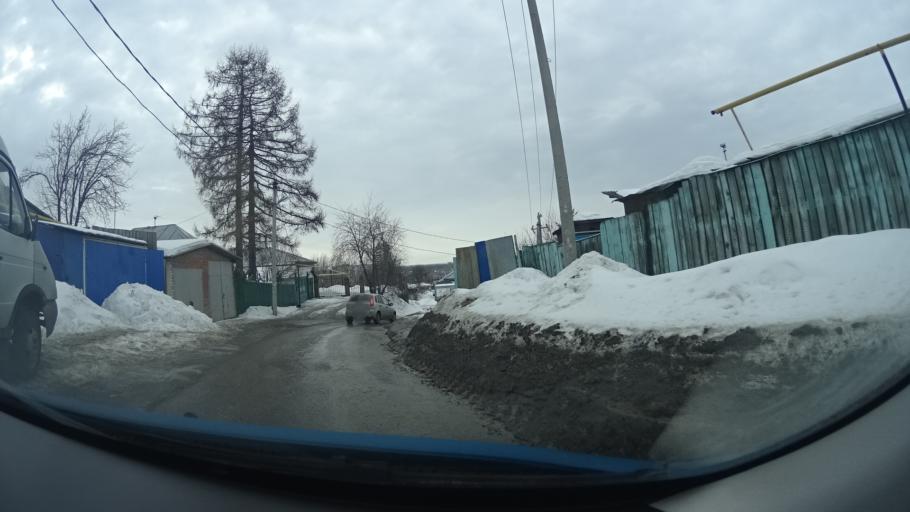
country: RU
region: Bashkortostan
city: Ufa
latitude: 54.6913
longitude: 55.9883
